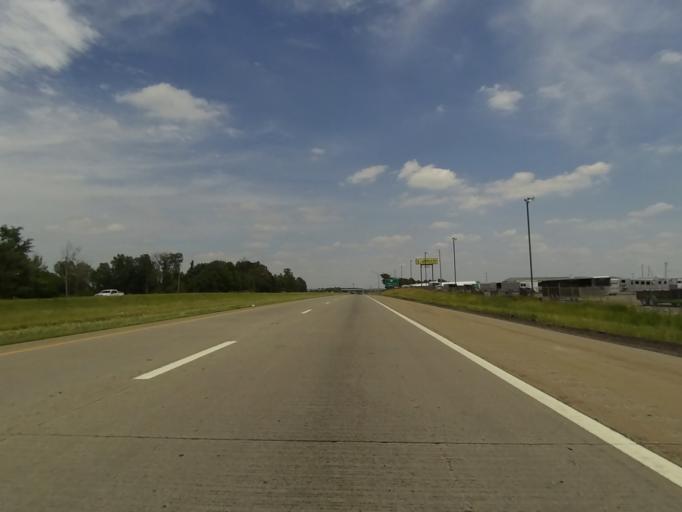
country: US
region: Ohio
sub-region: Trumbull County
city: Lordstown
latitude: 41.1066
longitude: -80.8963
